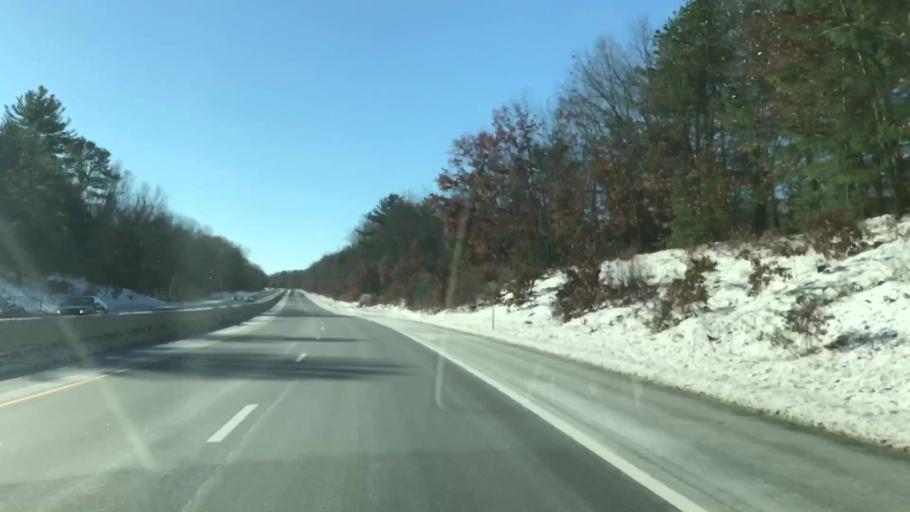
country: US
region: New Hampshire
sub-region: Hillsborough County
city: Pinardville
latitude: 43.0334
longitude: -71.4864
